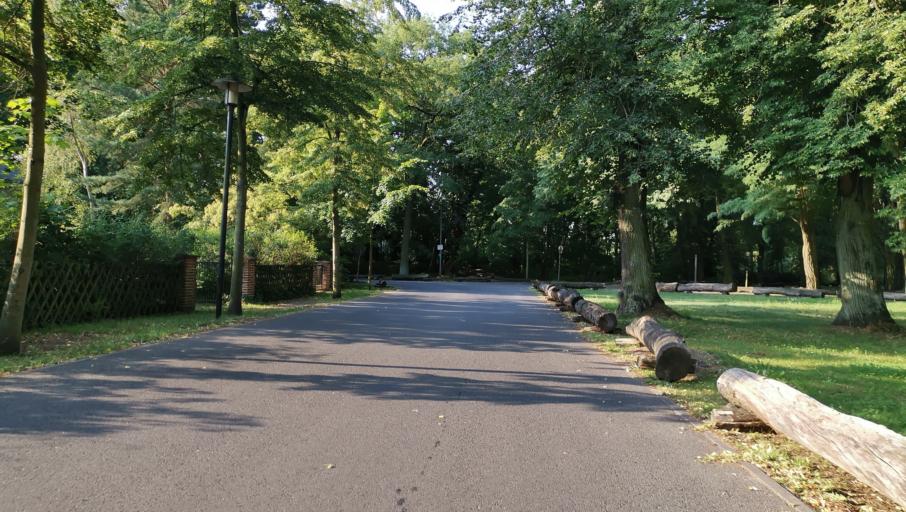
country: DE
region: Brandenburg
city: Potsdam
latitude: 52.3845
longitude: 13.0363
